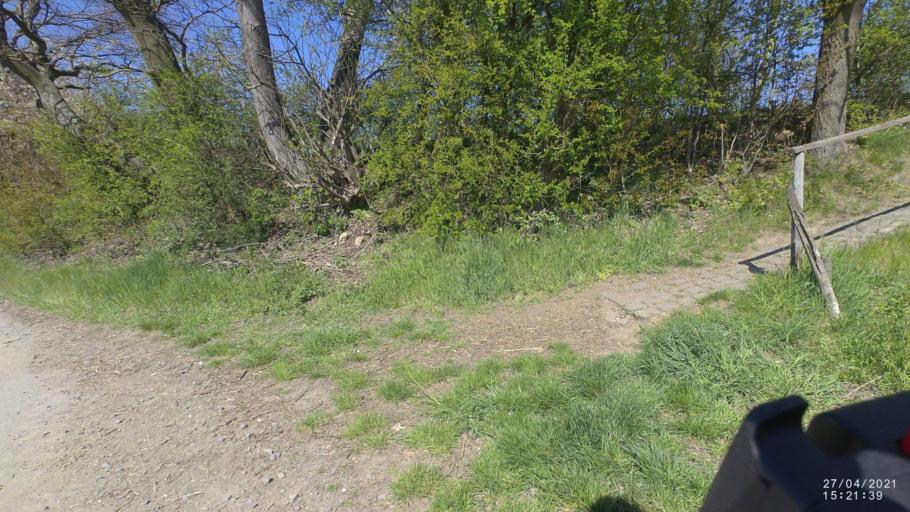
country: DE
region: Rheinland-Pfalz
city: Mertloch
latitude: 50.2643
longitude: 7.2999
